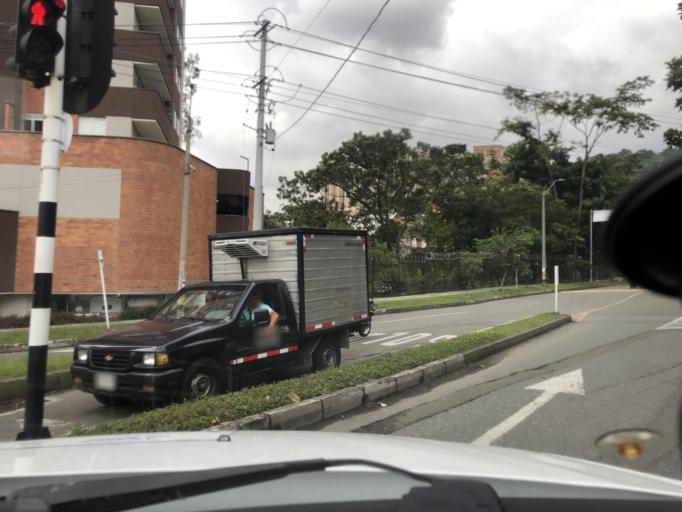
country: CO
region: Antioquia
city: Bello
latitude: 6.3233
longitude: -75.5638
